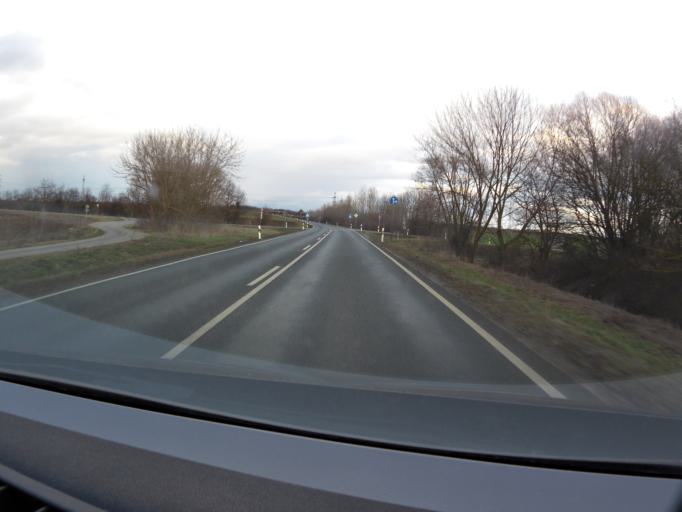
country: DE
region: Thuringia
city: Dornheim
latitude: 50.8503
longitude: 10.9981
